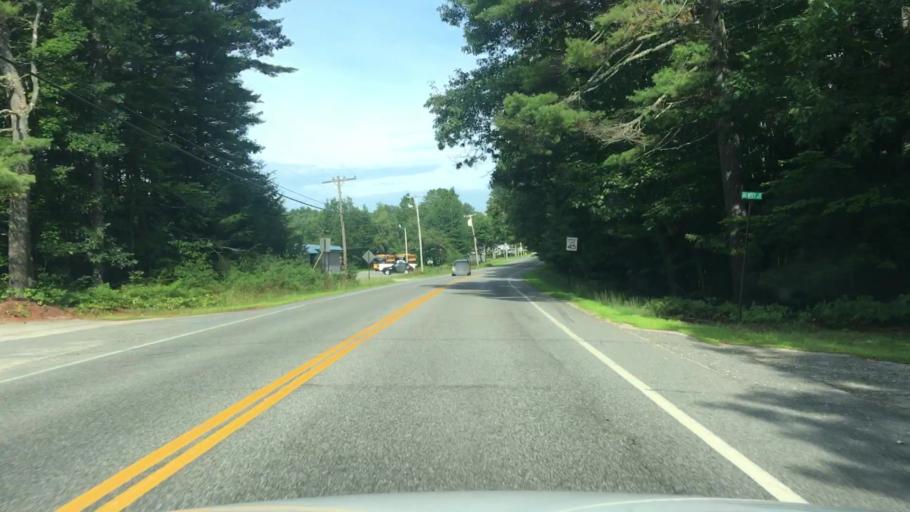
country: US
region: Maine
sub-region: York County
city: Cornish
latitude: 43.8033
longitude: -70.8631
